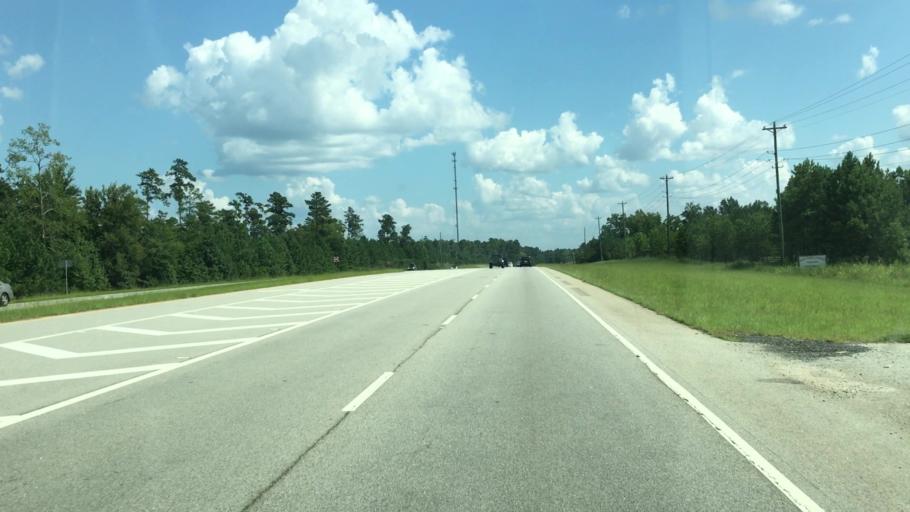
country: US
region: Georgia
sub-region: Putnam County
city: Eatonton
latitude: 33.2139
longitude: -83.3029
